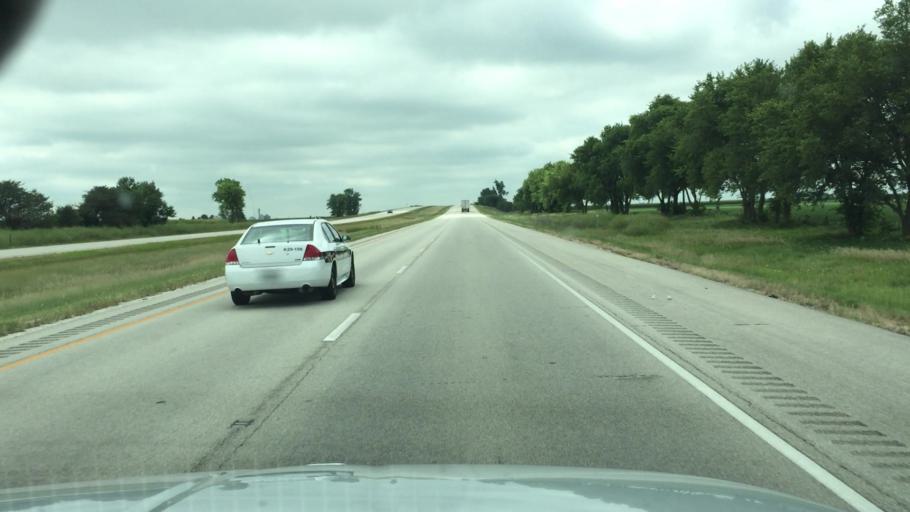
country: US
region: Illinois
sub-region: Henry County
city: Orion
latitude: 41.3576
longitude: -90.3313
